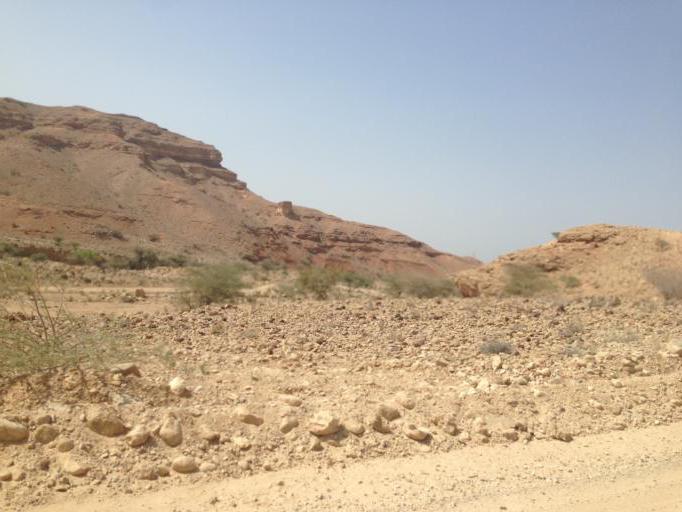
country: OM
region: Ash Sharqiyah
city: Ibra'
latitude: 23.0761
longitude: 58.8952
